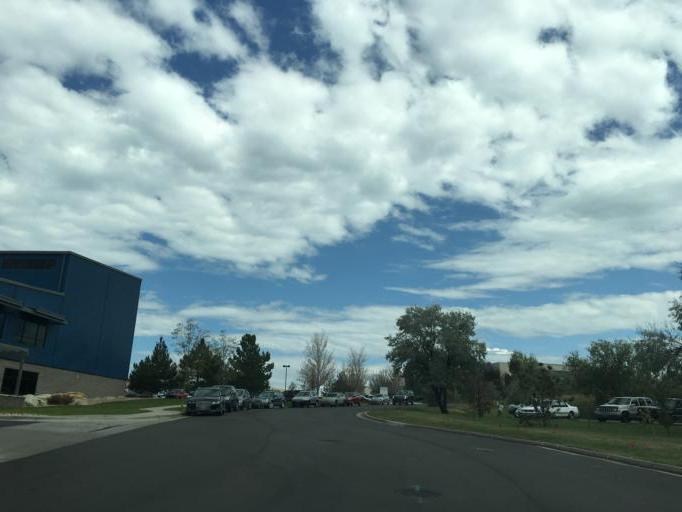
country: US
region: Colorado
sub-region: Jefferson County
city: West Pleasant View
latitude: 39.7278
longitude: -105.2081
